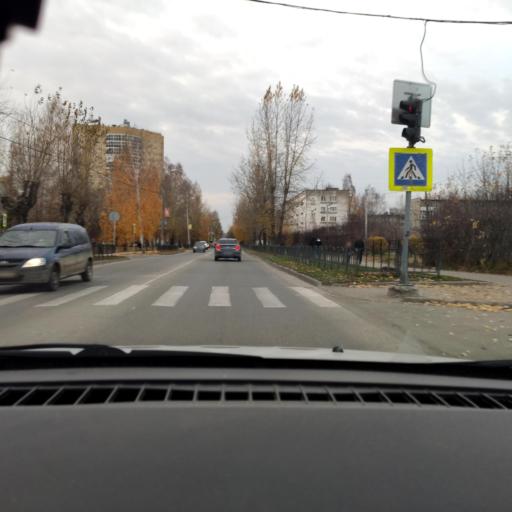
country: RU
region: Perm
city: Perm
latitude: 58.1062
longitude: 56.3822
